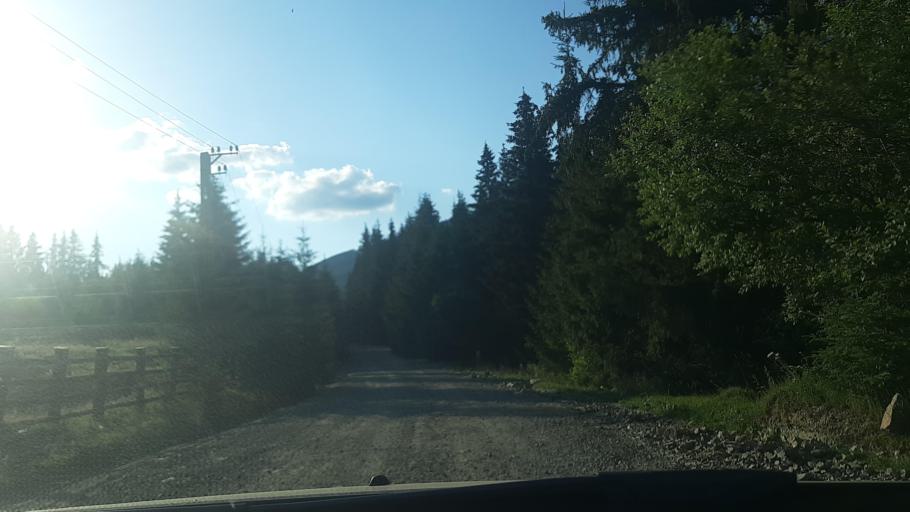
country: RO
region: Alba
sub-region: Comuna Sugag
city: Sugag
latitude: 45.5738
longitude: 23.6120
